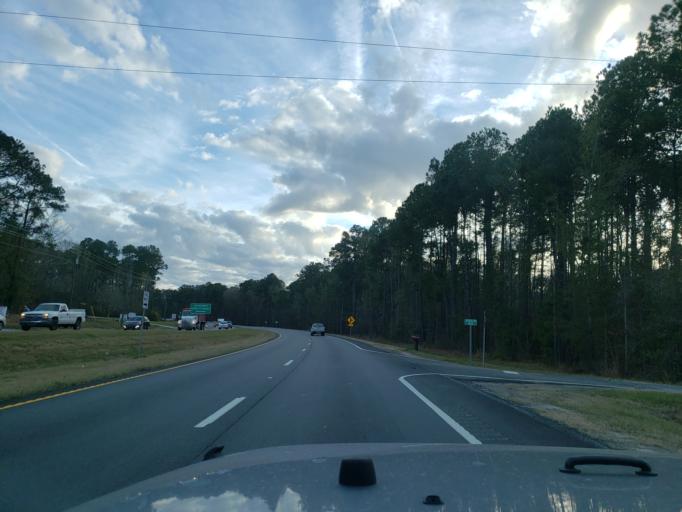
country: US
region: Georgia
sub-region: Chatham County
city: Port Wentworth
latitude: 32.2110
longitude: -81.2008
